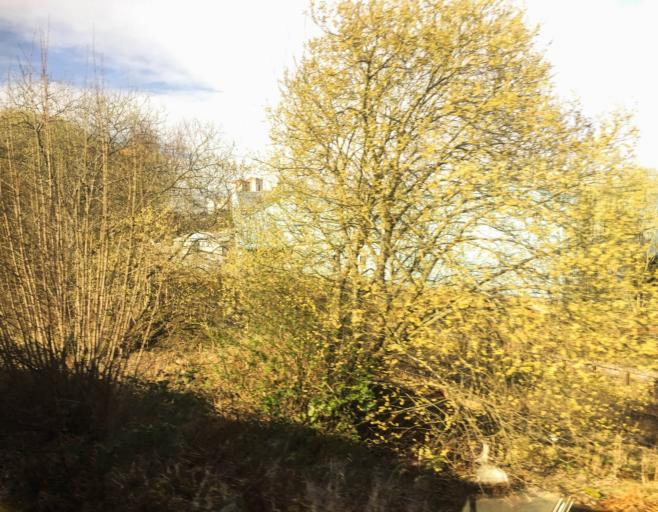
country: GB
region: Scotland
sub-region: East Dunbartonshire
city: Bishopbriggs
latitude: 55.8757
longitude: -4.2210
